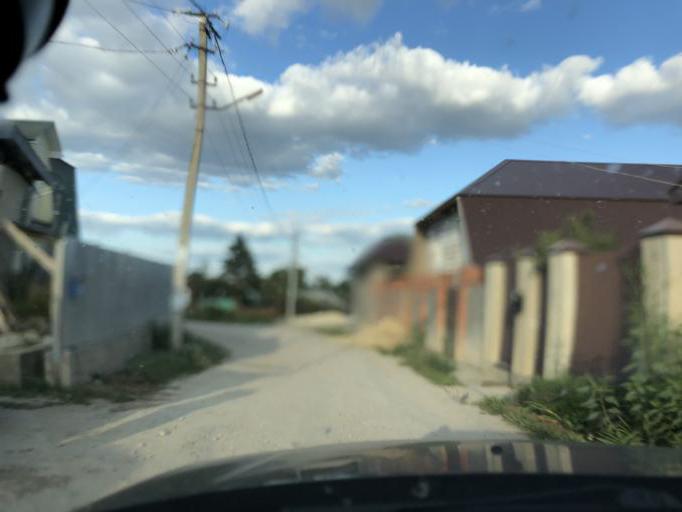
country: RU
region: Tula
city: Kosaya Gora
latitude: 54.1803
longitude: 37.5380
